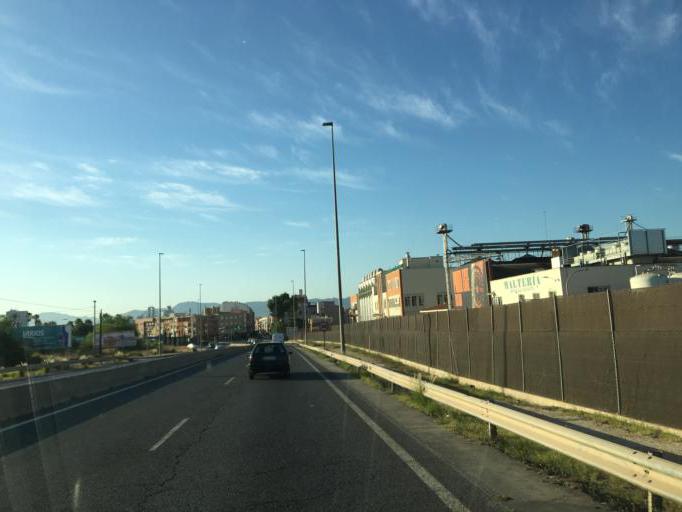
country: ES
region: Murcia
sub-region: Murcia
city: Murcia
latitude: 38.0156
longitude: -1.1581
